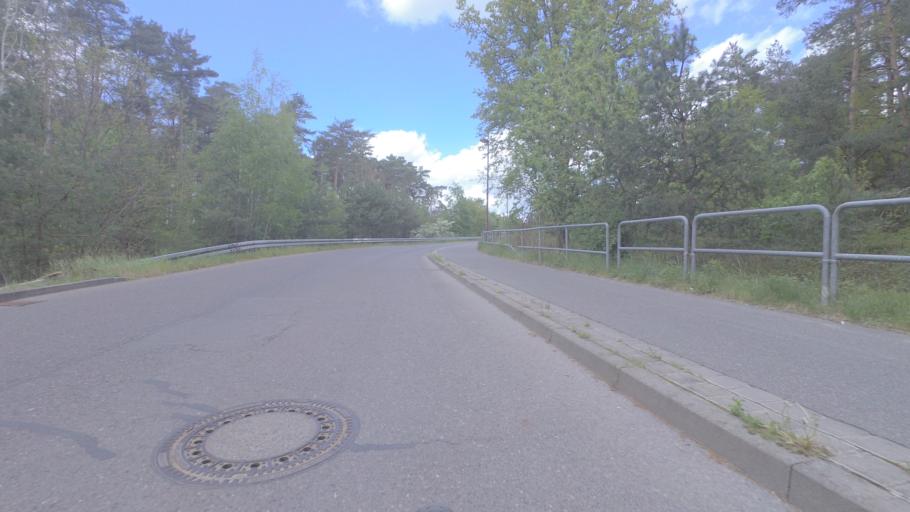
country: DE
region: Brandenburg
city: Ludwigsfelde
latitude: 52.2989
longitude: 13.2458
